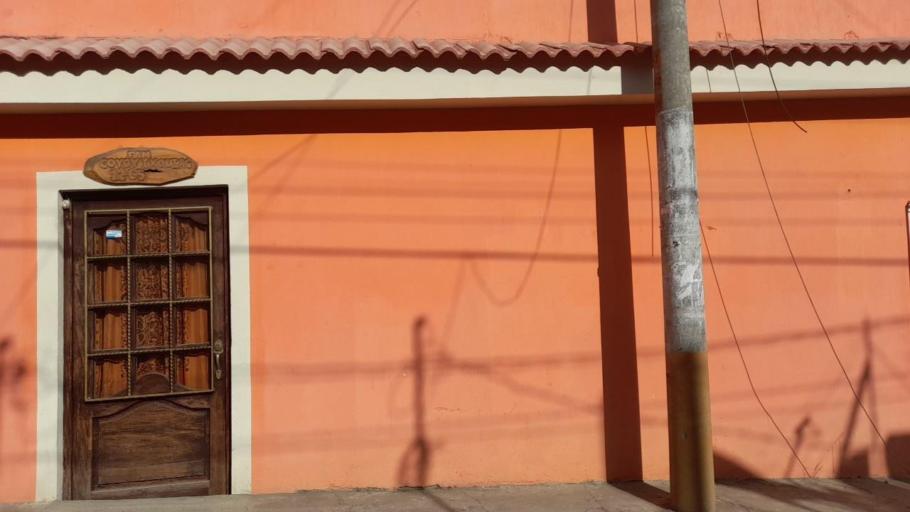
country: GT
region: Quetzaltenango
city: Quetzaltenango
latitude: 14.8275
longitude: -91.5156
